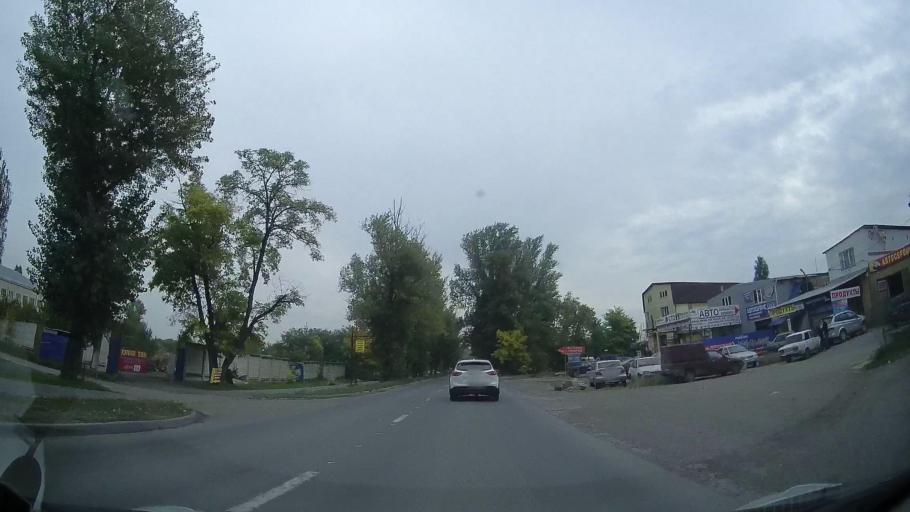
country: RU
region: Rostov
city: Severnyy
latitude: 47.2807
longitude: 39.6631
